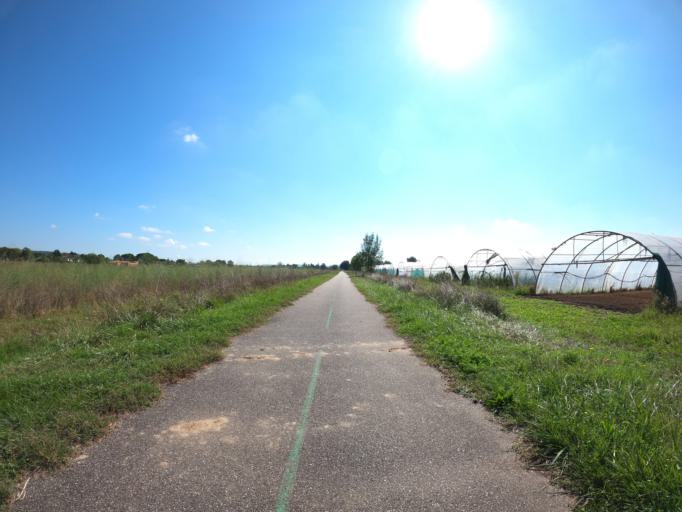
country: FR
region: Aquitaine
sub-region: Departement du Lot-et-Garonne
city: Casseneuil
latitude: 44.4356
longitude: 0.6351
